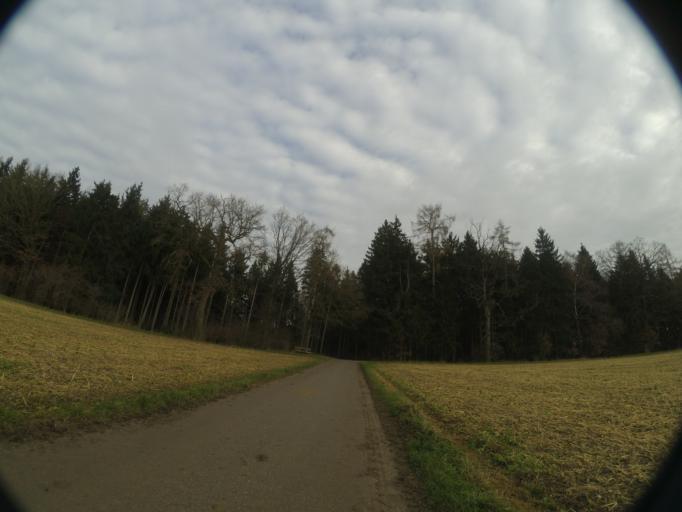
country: DE
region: Baden-Wuerttemberg
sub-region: Tuebingen Region
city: Erbach
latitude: 48.3626
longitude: 9.9246
